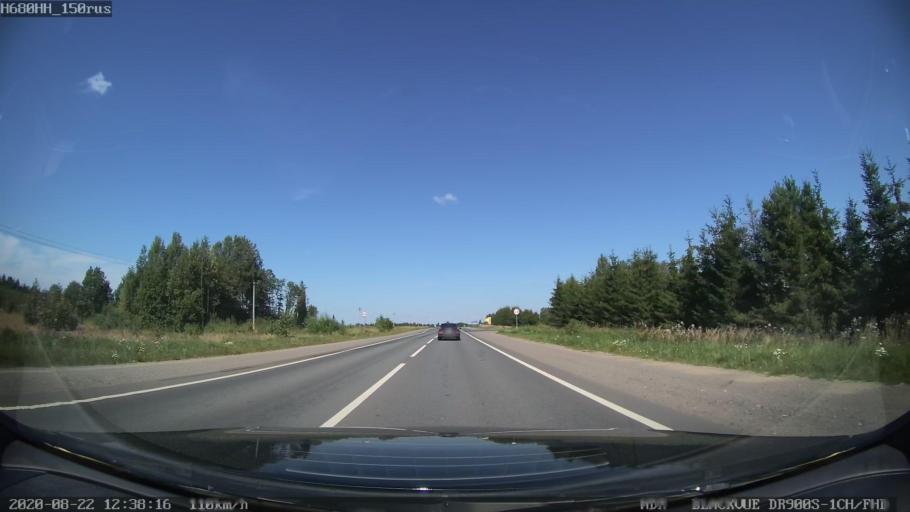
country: RU
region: Tverskaya
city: Rameshki
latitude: 57.3112
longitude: 36.0885
